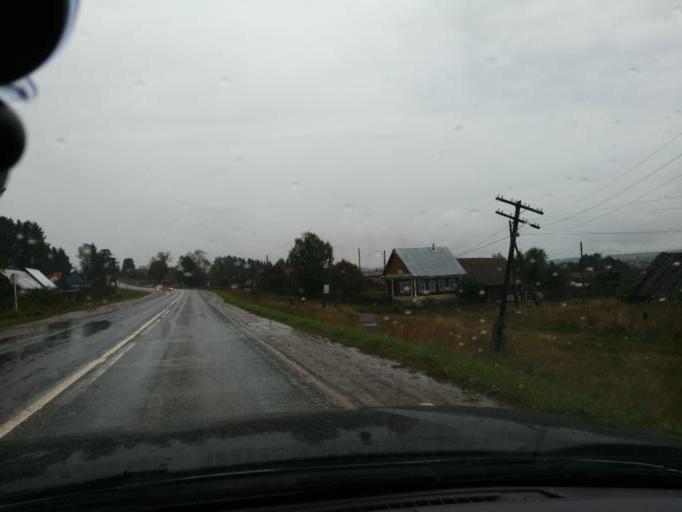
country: RU
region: Perm
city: Yugo-Kamskiy
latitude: 57.5514
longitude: 55.6854
